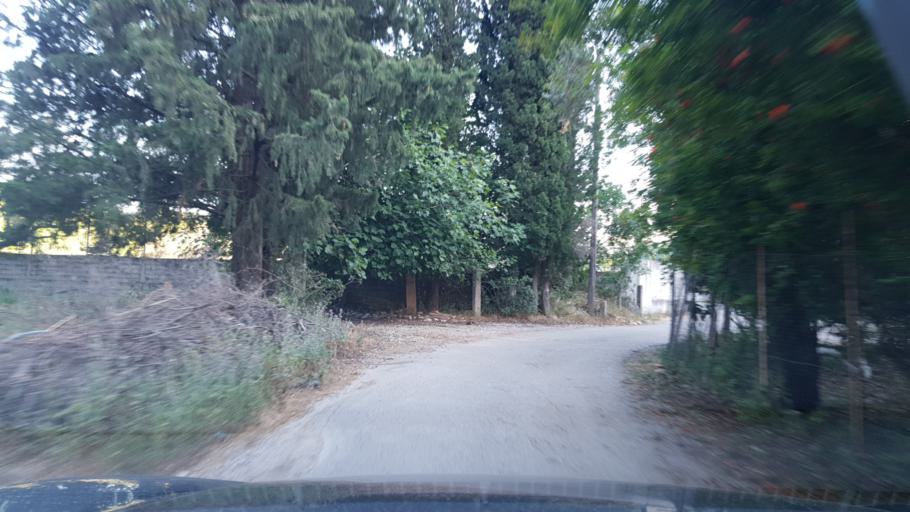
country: GR
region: Ionian Islands
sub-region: Lefkada
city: Nidri
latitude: 38.7193
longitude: 20.6951
